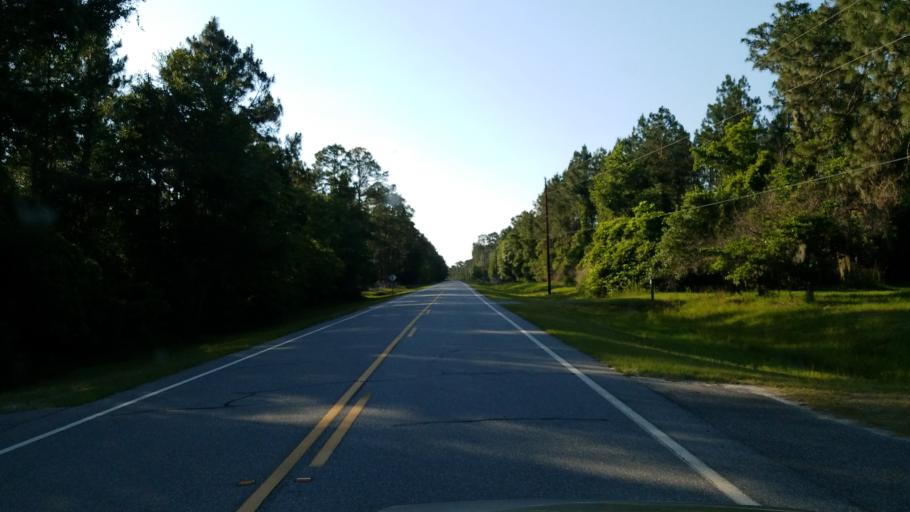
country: US
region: Georgia
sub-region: Lanier County
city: Lakeland
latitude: 30.8889
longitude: -83.0545
